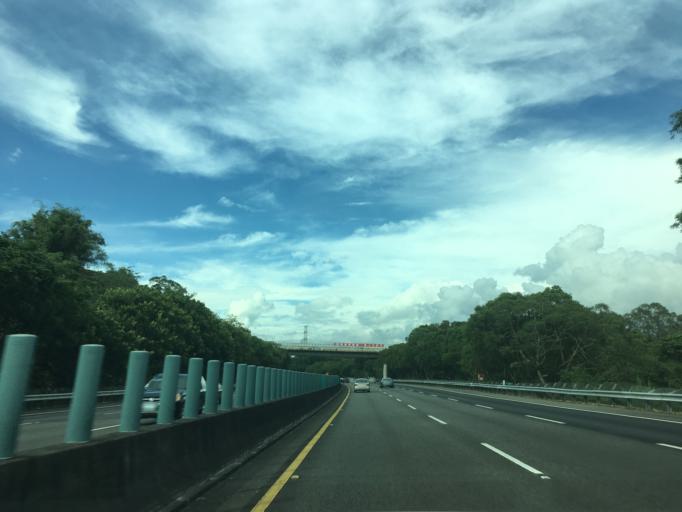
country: TW
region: Taiwan
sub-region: Chiayi
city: Jiayi Shi
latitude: 23.5404
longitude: 120.4976
